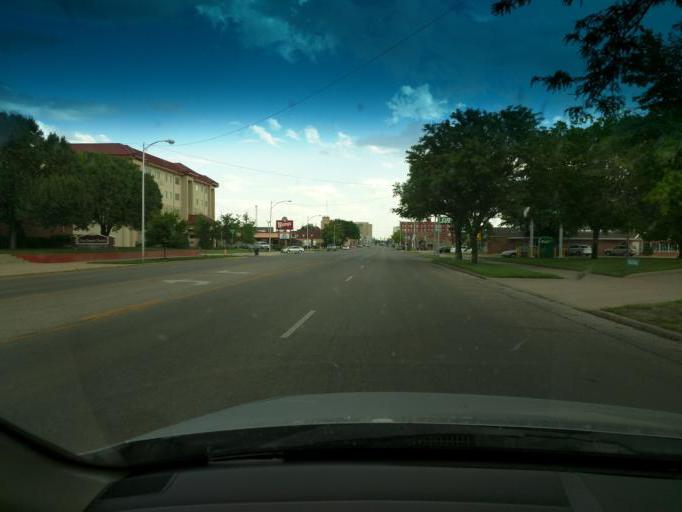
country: US
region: Kansas
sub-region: Reno County
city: Hutchinson
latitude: 38.0625
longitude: -97.9319
